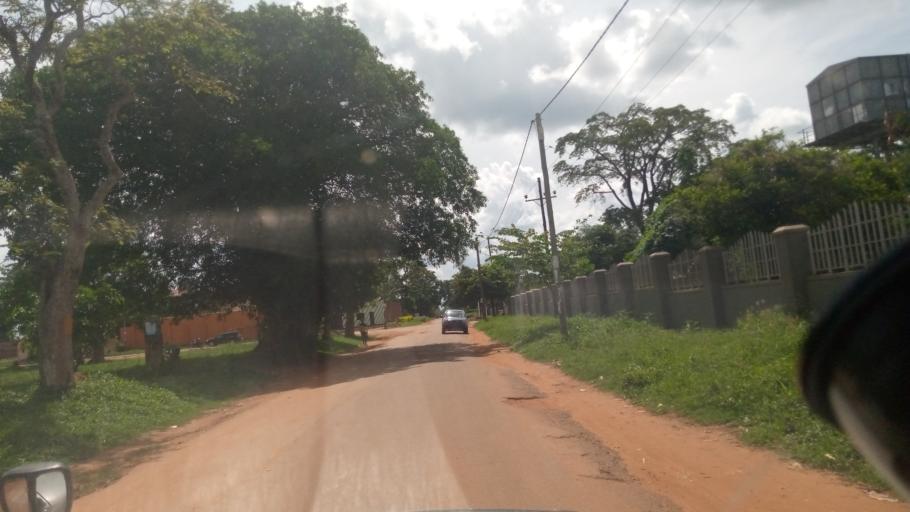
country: UG
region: Northern Region
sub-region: Lira District
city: Lira
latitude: 2.2511
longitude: 32.9011
